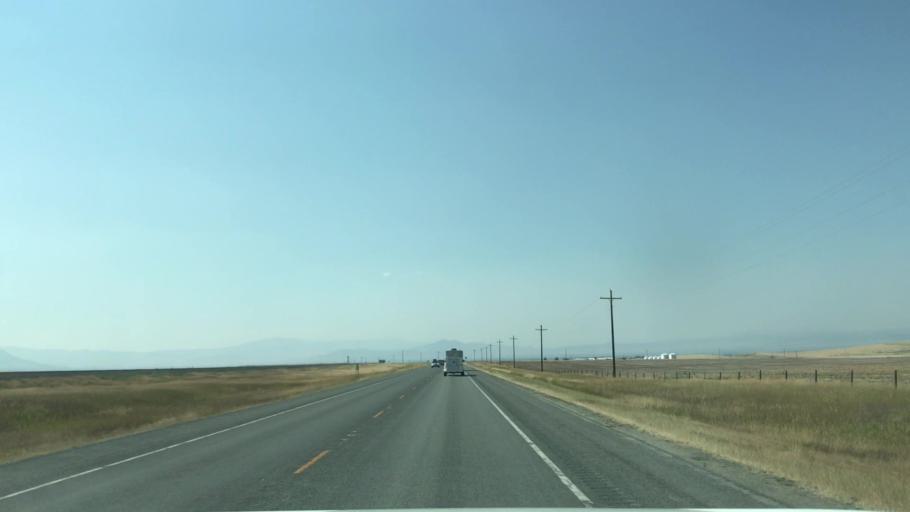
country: US
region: Montana
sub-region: Lewis and Clark County
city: East Helena
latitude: 46.5795
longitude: -111.8438
